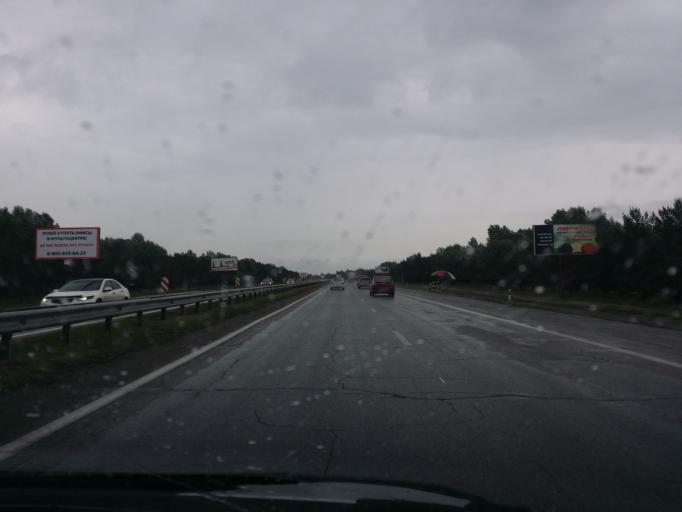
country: RU
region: Altai Krai
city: Zaton
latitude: 53.3150
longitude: 83.8483
